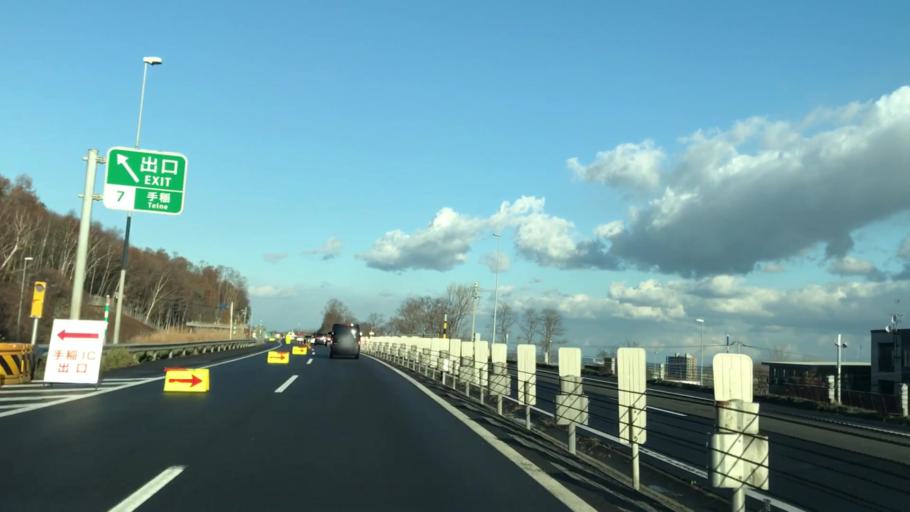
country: JP
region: Hokkaido
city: Sapporo
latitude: 43.1098
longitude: 141.2403
